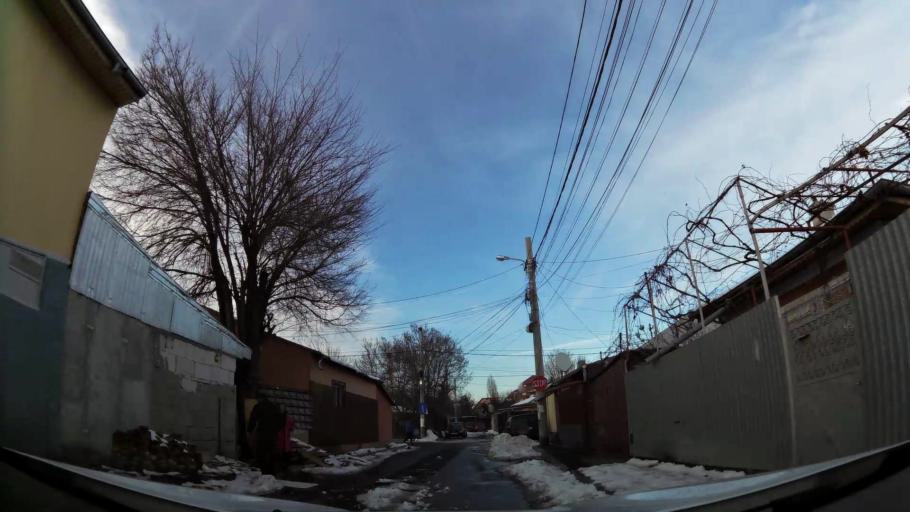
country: RO
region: Bucuresti
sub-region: Municipiul Bucuresti
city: Bucuresti
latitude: 44.3923
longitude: 26.0720
